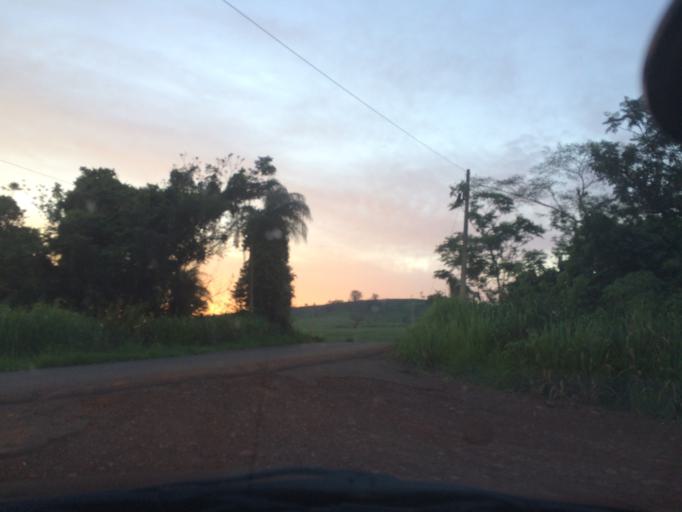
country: BR
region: Sao Paulo
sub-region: Tambau
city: Tambau
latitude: -21.7126
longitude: -47.1941
